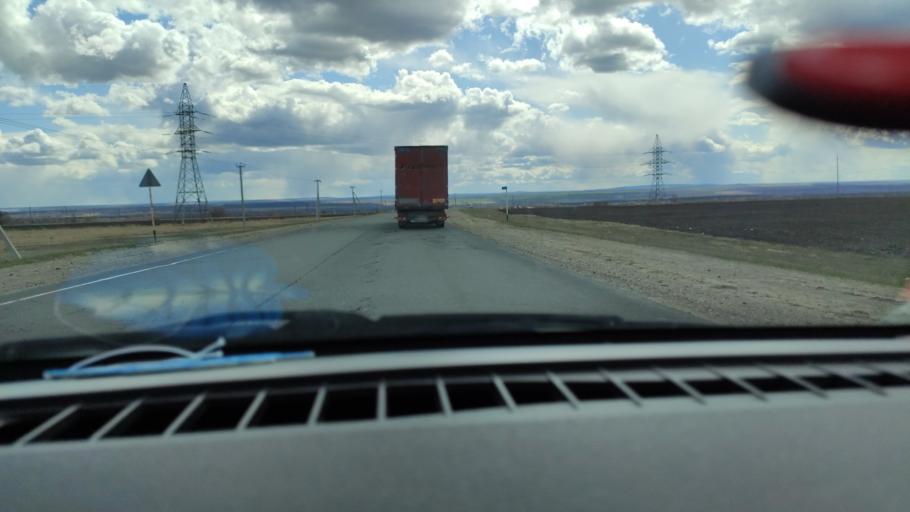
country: RU
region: Samara
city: Varlamovo
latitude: 53.1838
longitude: 48.2892
